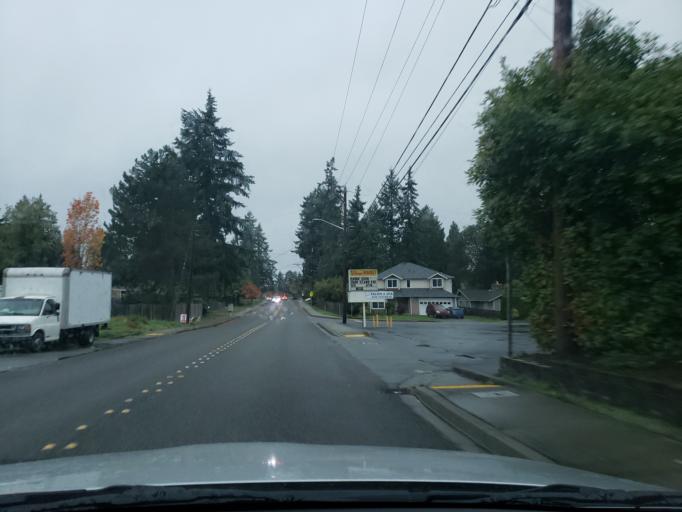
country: US
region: Washington
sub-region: Snohomish County
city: Lynnwood
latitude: 47.8392
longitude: -122.3163
